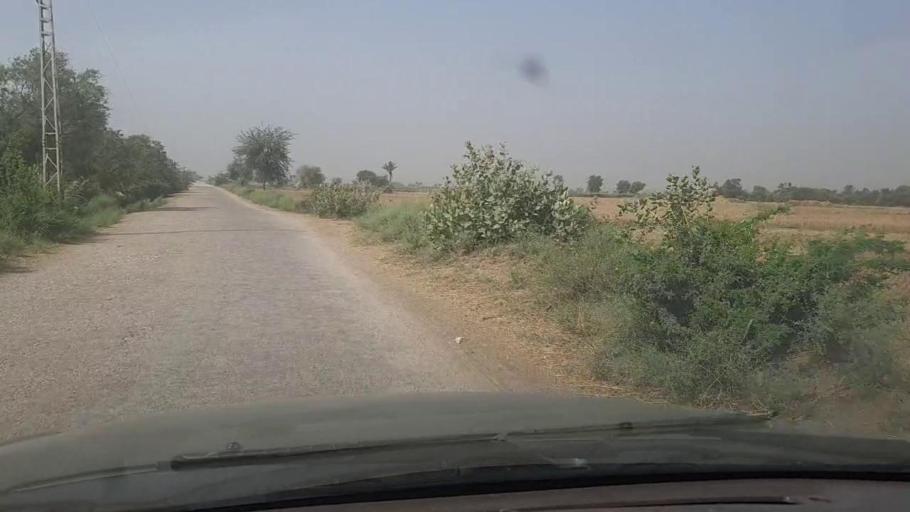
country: PK
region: Sindh
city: Garhi Yasin
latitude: 27.8600
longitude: 68.5479
